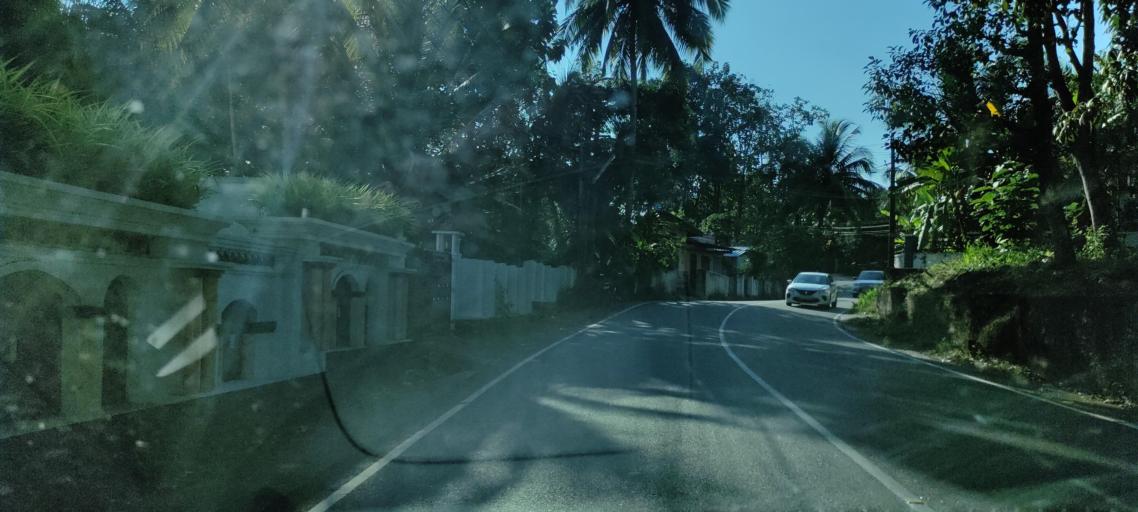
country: IN
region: Kerala
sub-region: Pattanamtitta
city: Pathanamthitta
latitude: 9.2224
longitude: 76.7512
